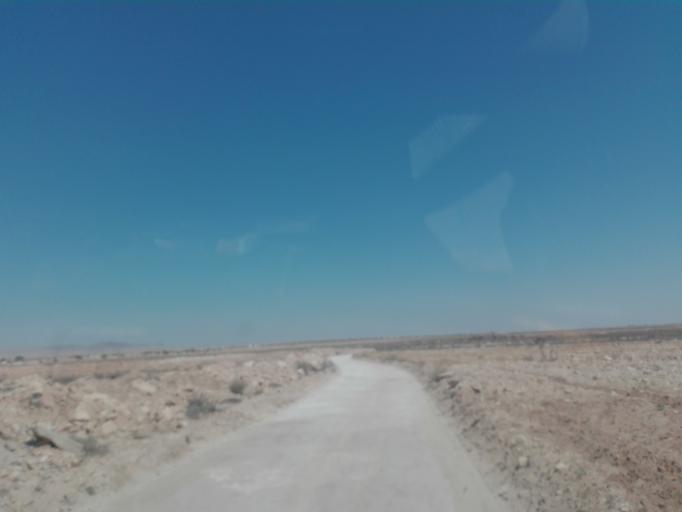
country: TN
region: Safaqis
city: Skhira
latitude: 34.4156
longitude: 9.9513
